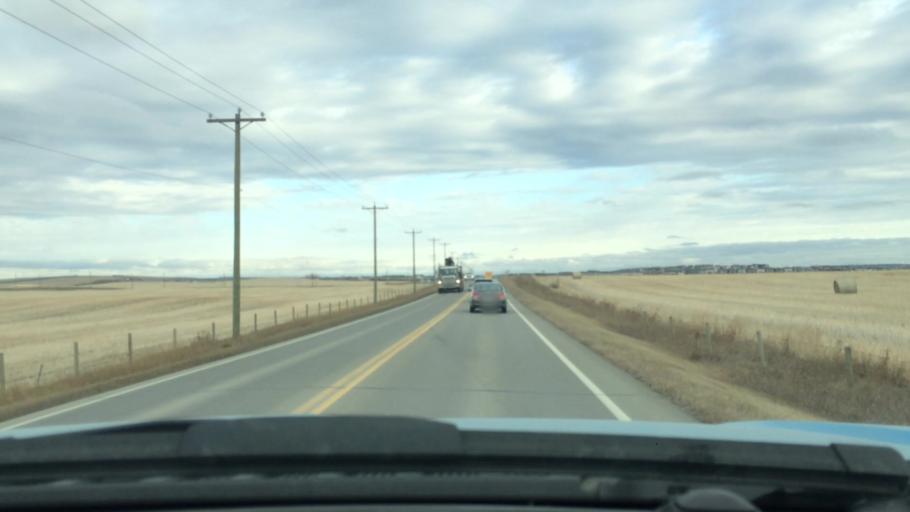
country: CA
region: Alberta
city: Airdrie
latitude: 51.2360
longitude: -114.0250
